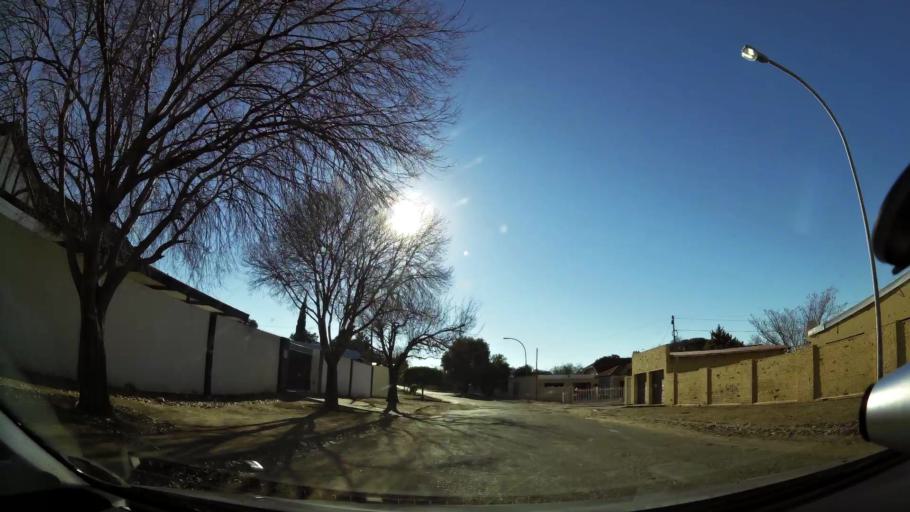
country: ZA
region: Northern Cape
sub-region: Frances Baard District Municipality
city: Kimberley
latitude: -28.7528
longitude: 24.7808
